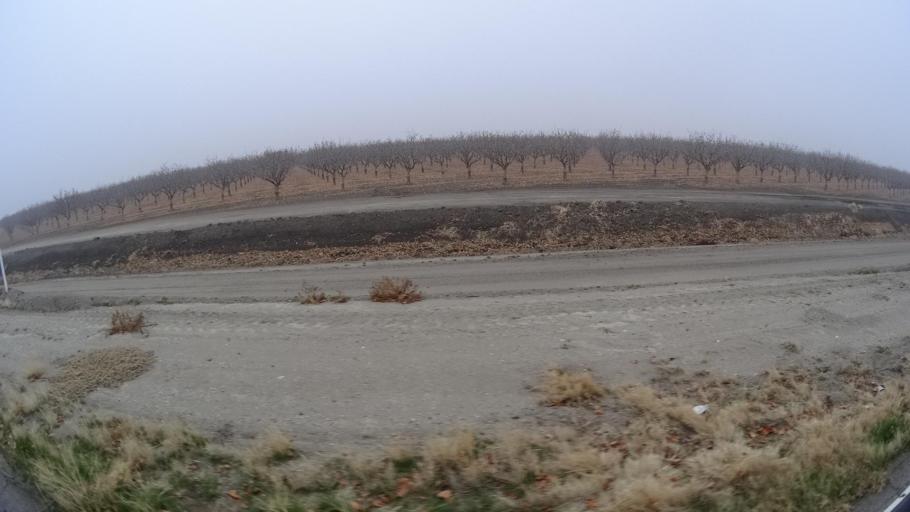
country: US
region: California
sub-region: Kern County
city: Buttonwillow
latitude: 35.4220
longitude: -119.5254
